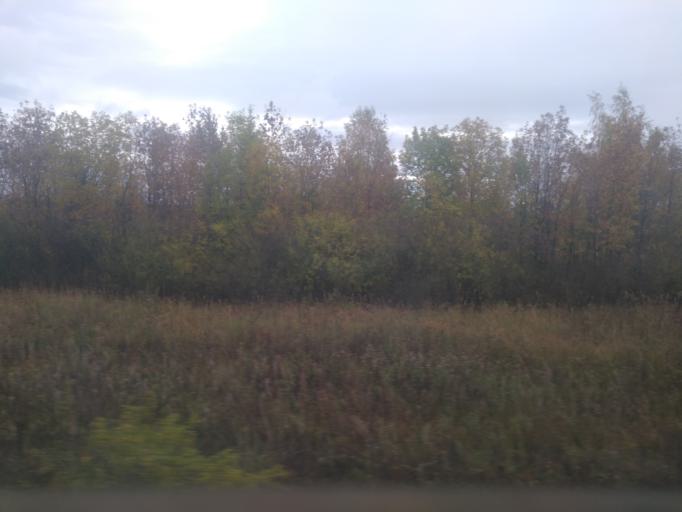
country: RU
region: Udmurtiya
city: Alnashi
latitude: 56.2100
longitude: 52.6245
